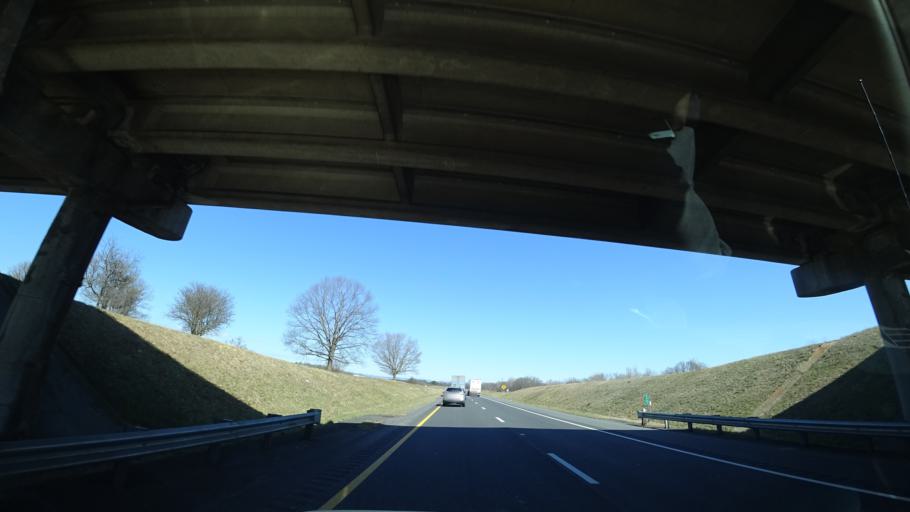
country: US
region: Virginia
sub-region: Shenandoah County
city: Mount Jackson
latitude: 38.7046
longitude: -78.6562
